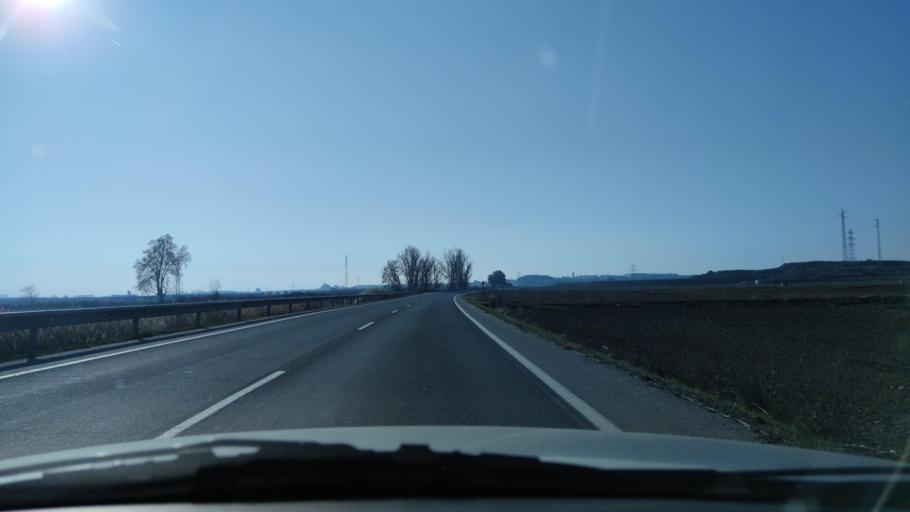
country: ES
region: Catalonia
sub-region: Provincia de Lleida
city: Albesa
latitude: 41.7131
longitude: 0.6393
